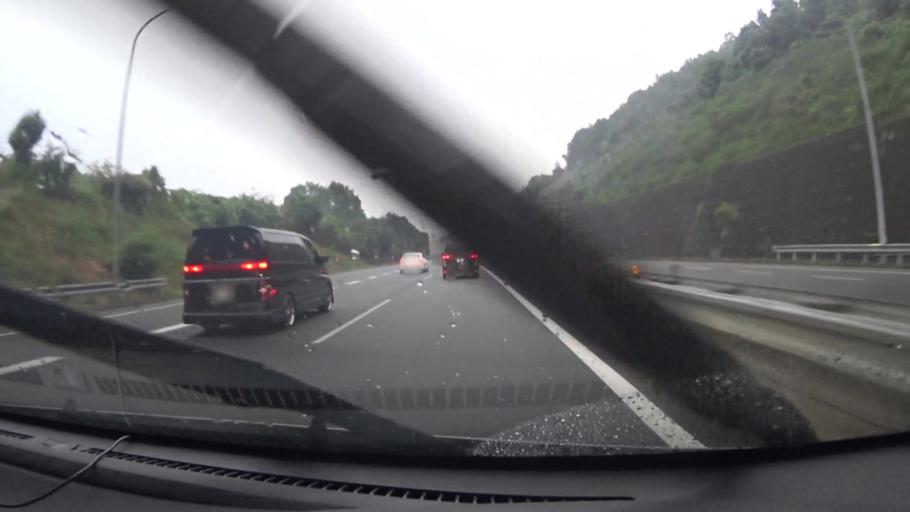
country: JP
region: Kyoto
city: Kameoka
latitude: 35.0059
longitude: 135.5643
